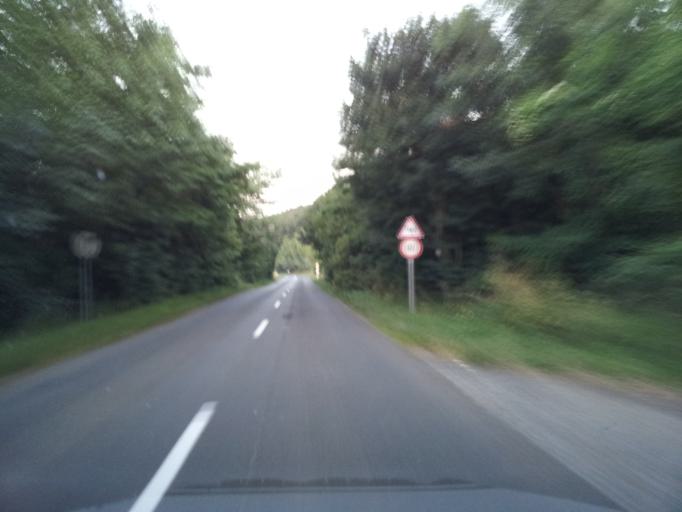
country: HU
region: Fejer
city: Szarliget
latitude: 47.5212
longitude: 18.5175
